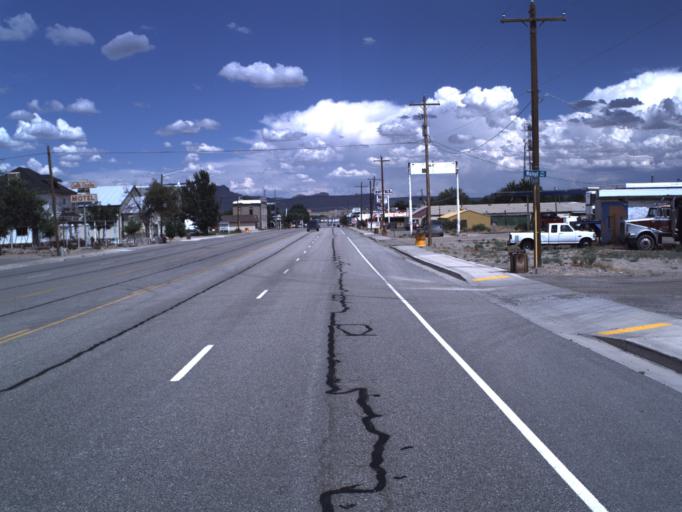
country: US
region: Utah
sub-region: Carbon County
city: East Carbon City
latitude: 38.9954
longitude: -110.1690
